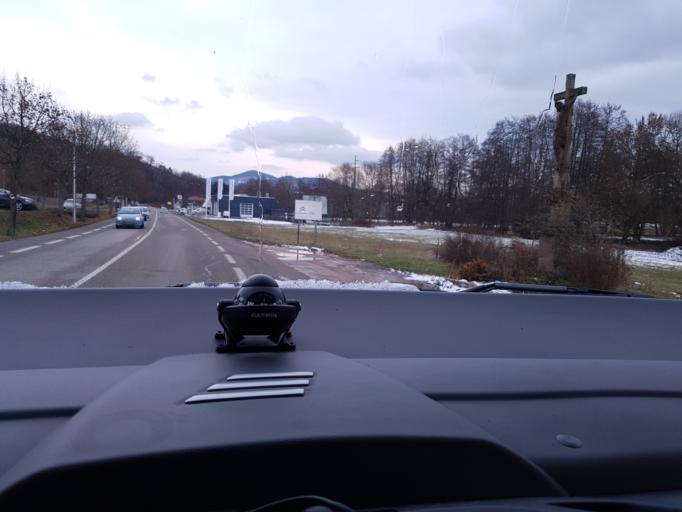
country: FR
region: Alsace
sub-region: Departement du Bas-Rhin
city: Ville
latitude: 48.3408
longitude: 7.3111
